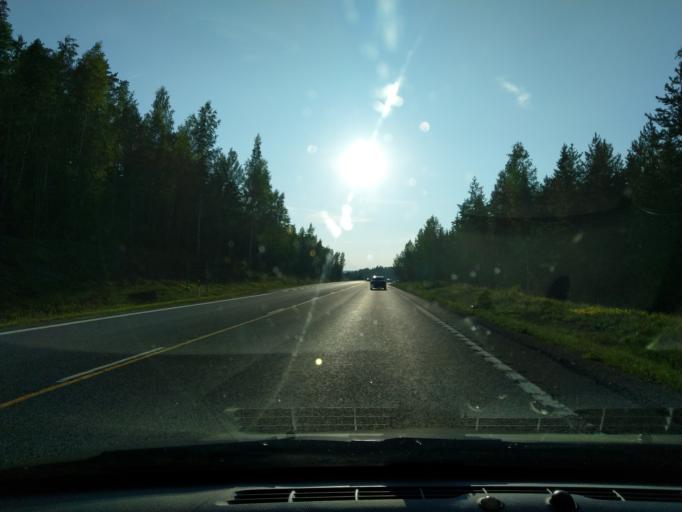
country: FI
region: Paijanne Tavastia
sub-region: Lahti
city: Lahti
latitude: 60.9672
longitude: 25.7360
